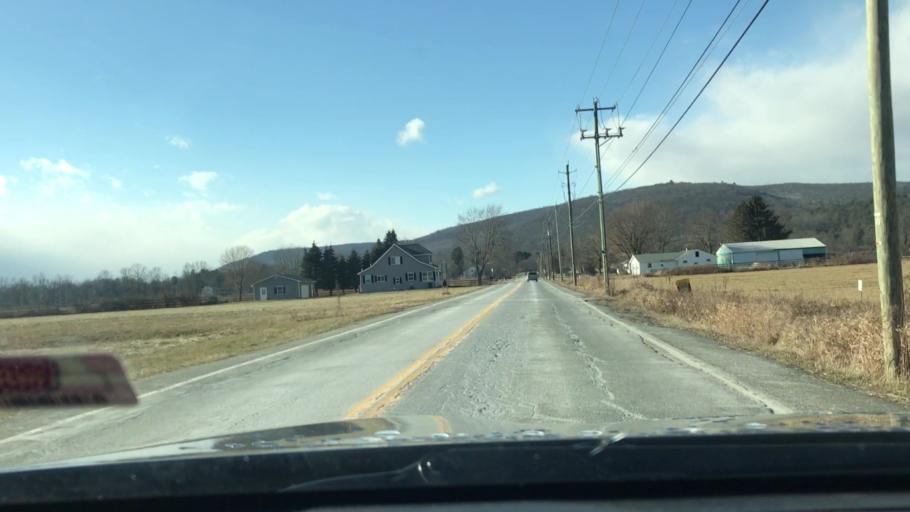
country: US
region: New York
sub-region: Chemung County
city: Big Flats
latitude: 42.1590
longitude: -76.9083
